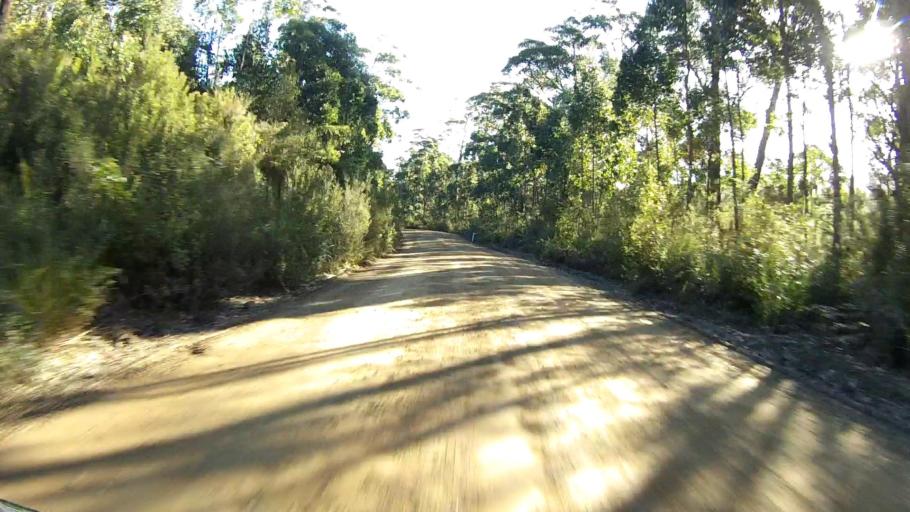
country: AU
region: Tasmania
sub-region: Clarence
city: Sandford
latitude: -43.1167
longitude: 147.9144
